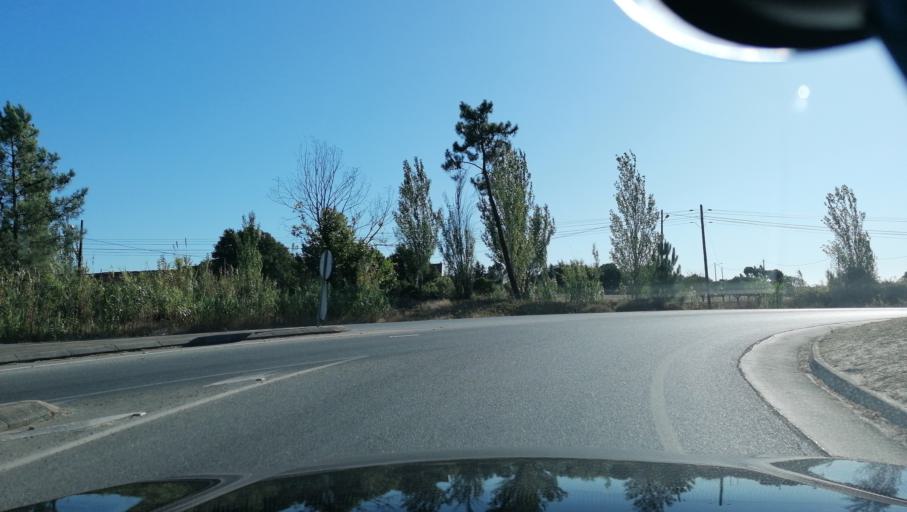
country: PT
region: Setubal
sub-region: Moita
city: Moita
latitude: 38.6353
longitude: -8.9712
